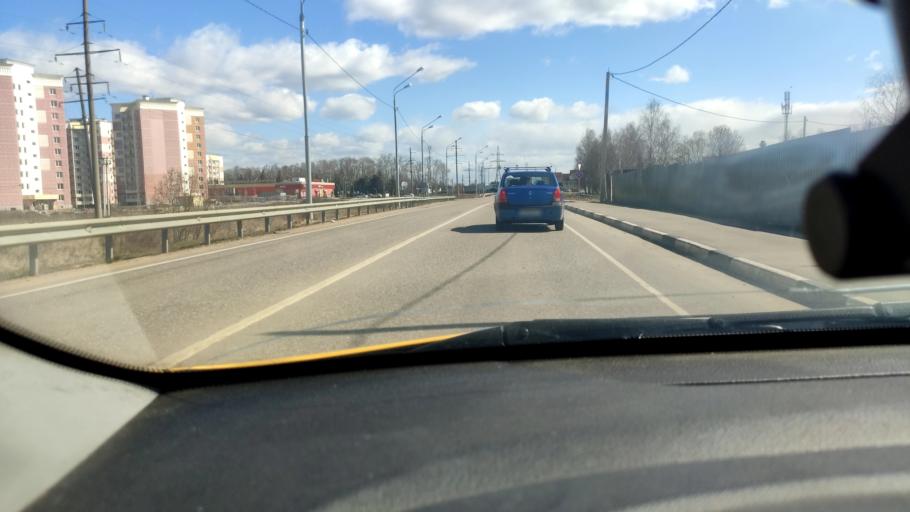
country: RU
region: Moskovskaya
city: Ruza
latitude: 55.7101
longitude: 36.1985
